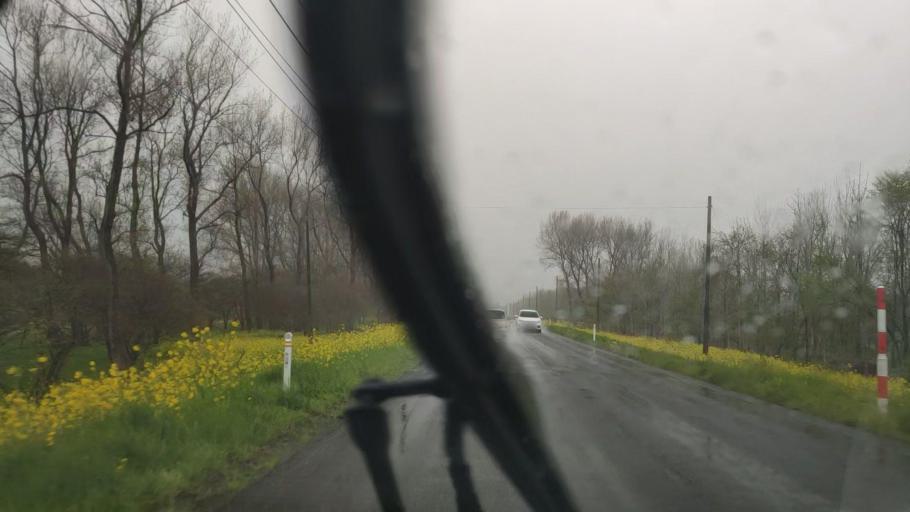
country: JP
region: Akita
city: Tenno
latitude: 39.9545
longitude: 139.9459
